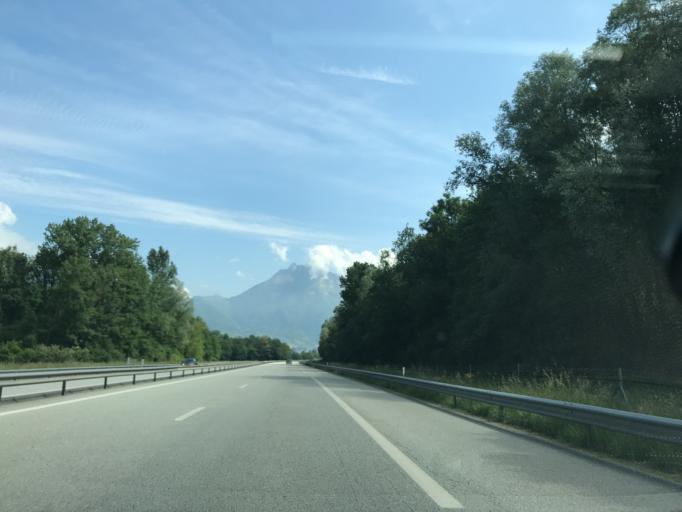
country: FR
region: Rhone-Alpes
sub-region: Departement de la Savoie
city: Cruet
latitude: 45.5194
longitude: 6.1110
